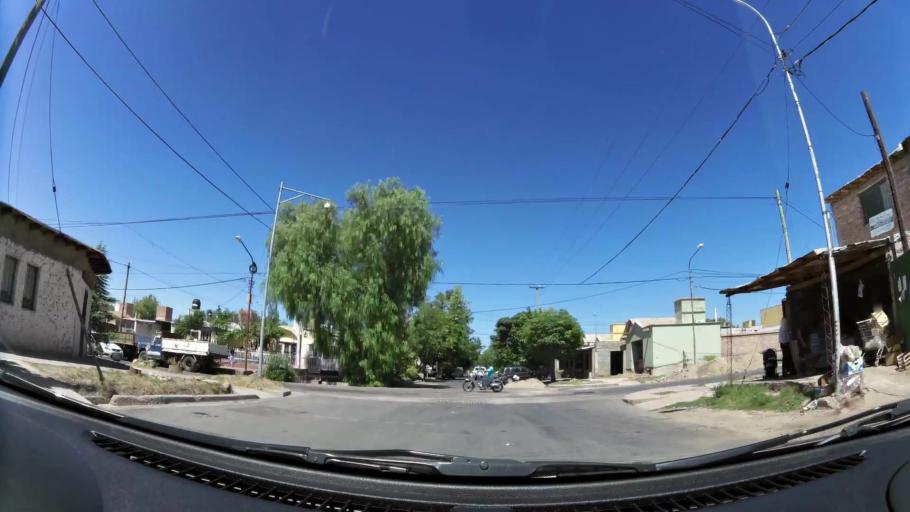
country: AR
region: Mendoza
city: Las Heras
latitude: -32.8381
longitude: -68.8723
